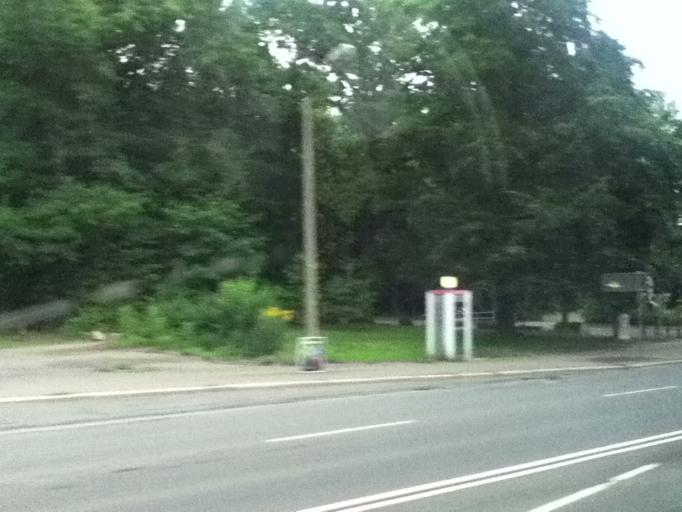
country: DE
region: Saxony
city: Chemnitz
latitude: 50.8474
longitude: 12.8998
